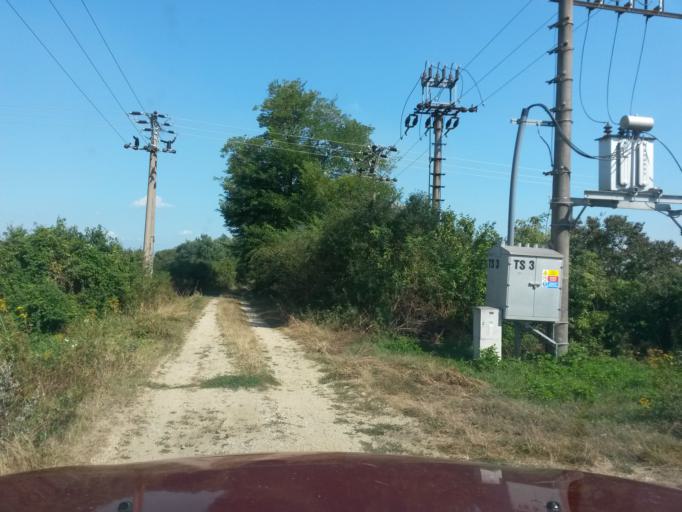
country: HU
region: Borsod-Abauj-Zemplen
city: Gonc
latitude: 48.5369
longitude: 21.1564
